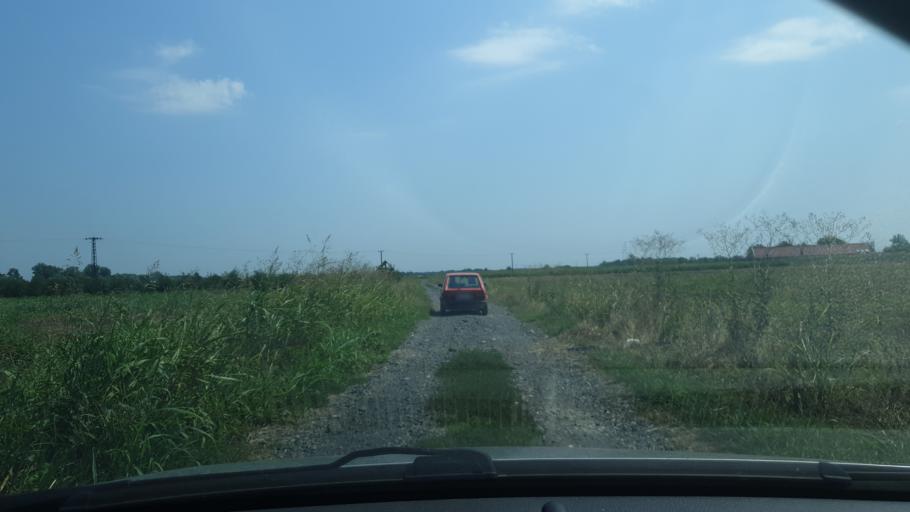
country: RS
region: Autonomna Pokrajina Vojvodina
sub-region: Sremski Okrug
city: Sremska Mitrovica
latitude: 44.9544
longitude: 19.6120
